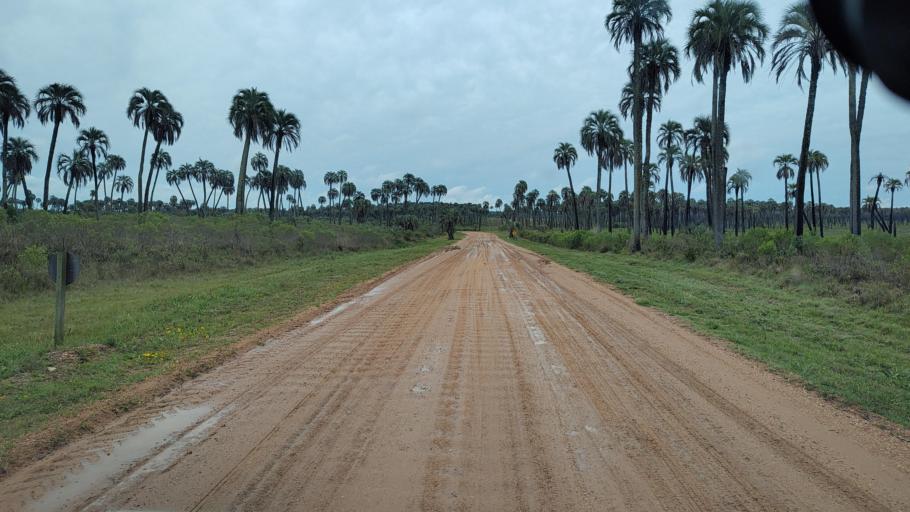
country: AR
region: Entre Rios
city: Ubajay
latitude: -31.8538
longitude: -58.3177
